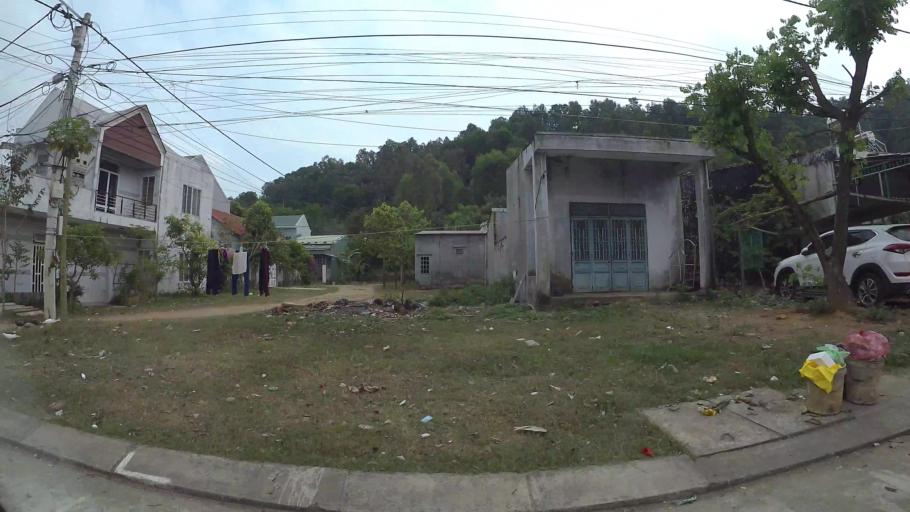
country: VN
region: Da Nang
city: Cam Le
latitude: 16.0318
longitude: 108.1772
